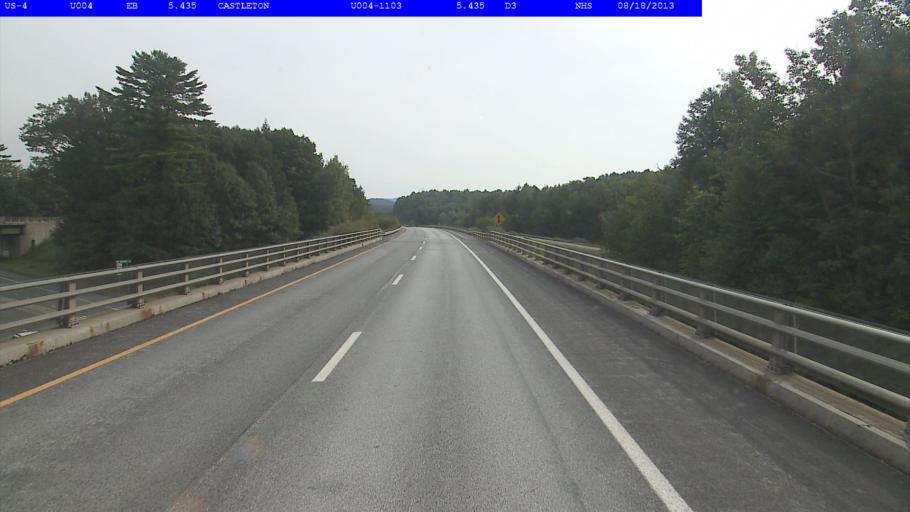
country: US
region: Vermont
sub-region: Rutland County
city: Castleton
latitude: 43.6161
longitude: -73.2070
